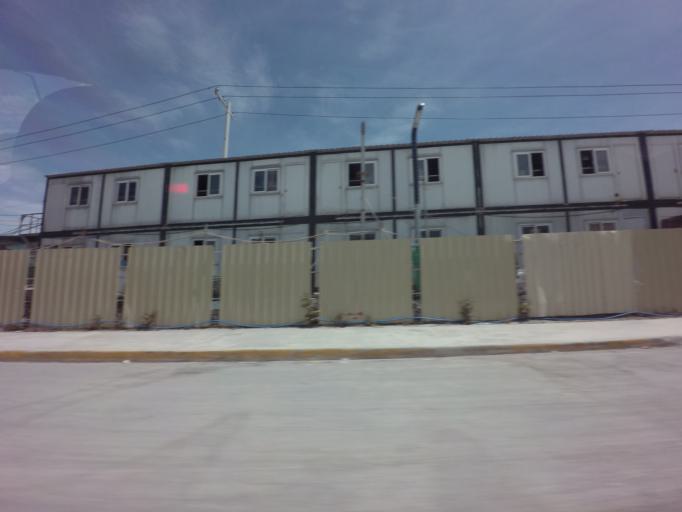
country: PH
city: Sambayanihan People's Village
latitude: 14.5110
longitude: 120.9814
